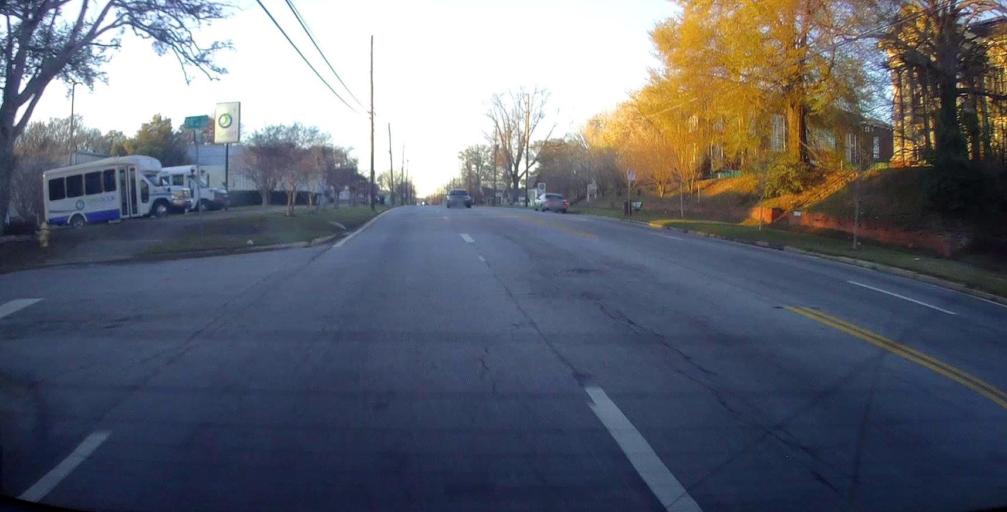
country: US
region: Alabama
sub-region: Russell County
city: Phenix City
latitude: 32.4865
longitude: -84.9902
